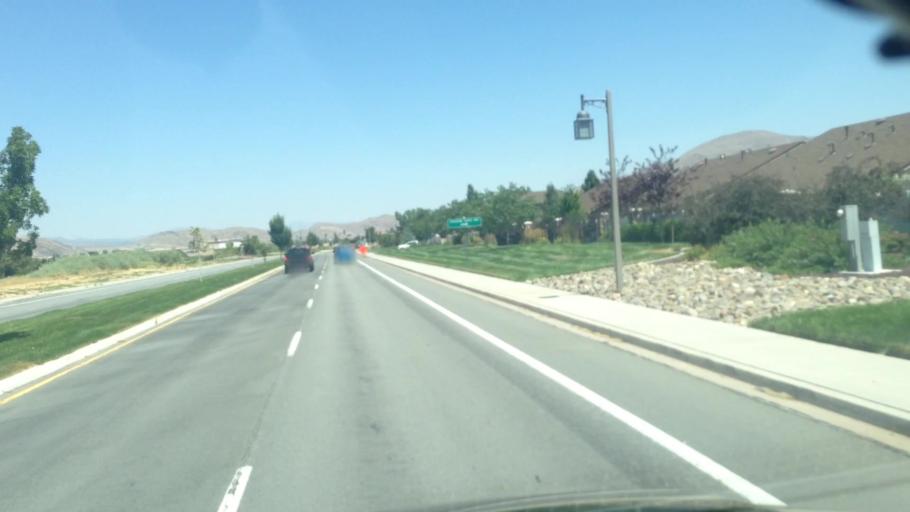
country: US
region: Nevada
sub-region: Washoe County
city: Sparks
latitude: 39.4129
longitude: -119.7333
